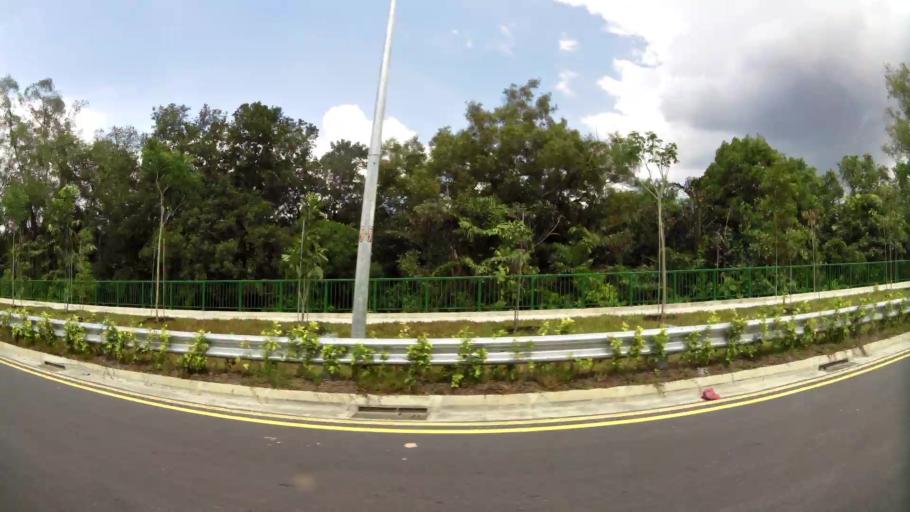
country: MY
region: Johor
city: Kampung Pasir Gudang Baru
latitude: 1.4336
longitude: 103.8481
